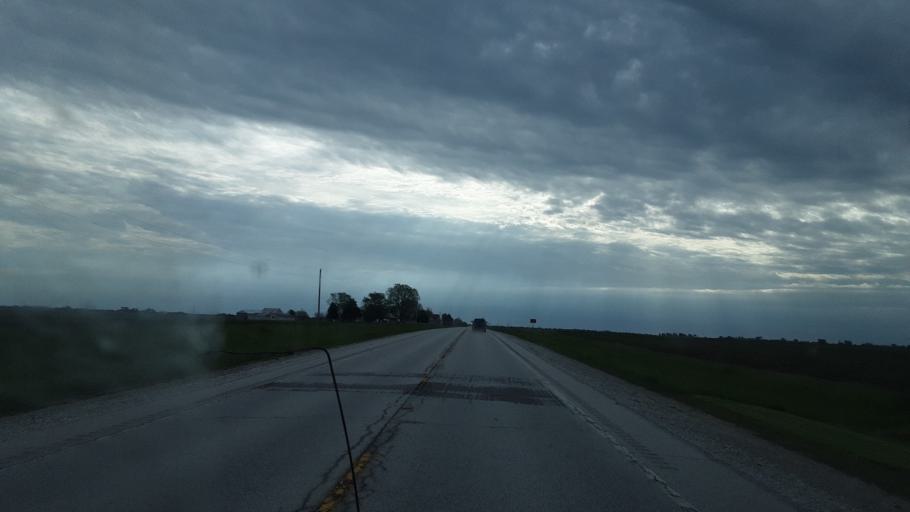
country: US
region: Illinois
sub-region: Hancock County
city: Carthage
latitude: 40.4008
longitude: -91.2029
